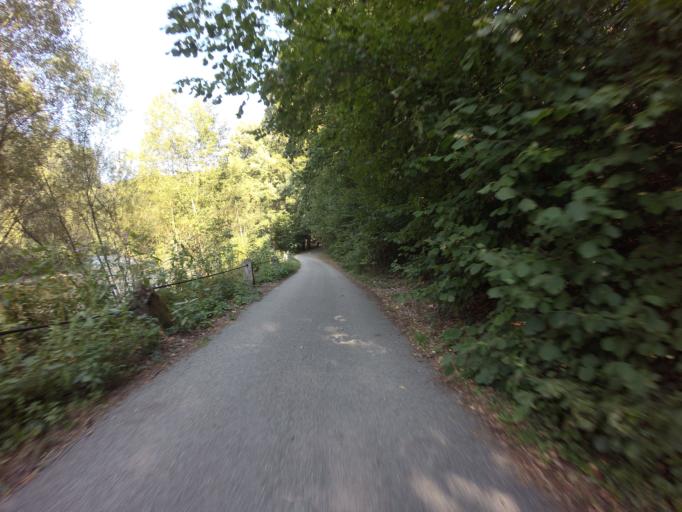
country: CZ
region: Jihocesky
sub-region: Okres Cesky Krumlov
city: Cesky Krumlov
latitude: 48.8576
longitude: 14.3736
